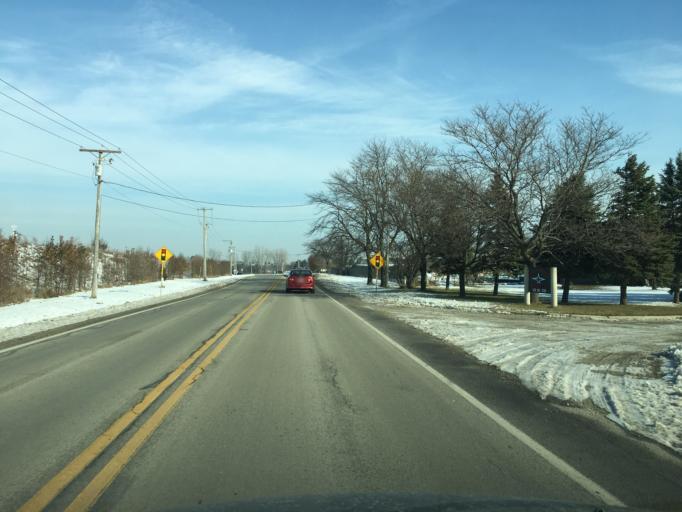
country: US
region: Illinois
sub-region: Will County
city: Plainfield
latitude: 41.6786
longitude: -88.1686
